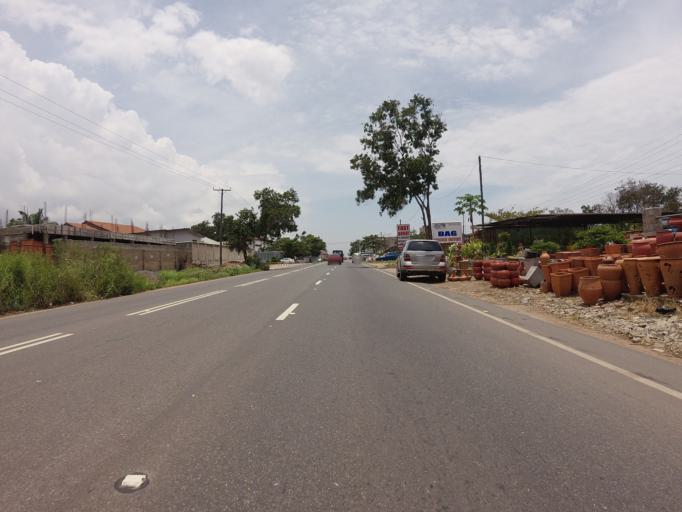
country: GH
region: Greater Accra
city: Medina Estates
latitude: 5.6338
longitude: -0.1484
